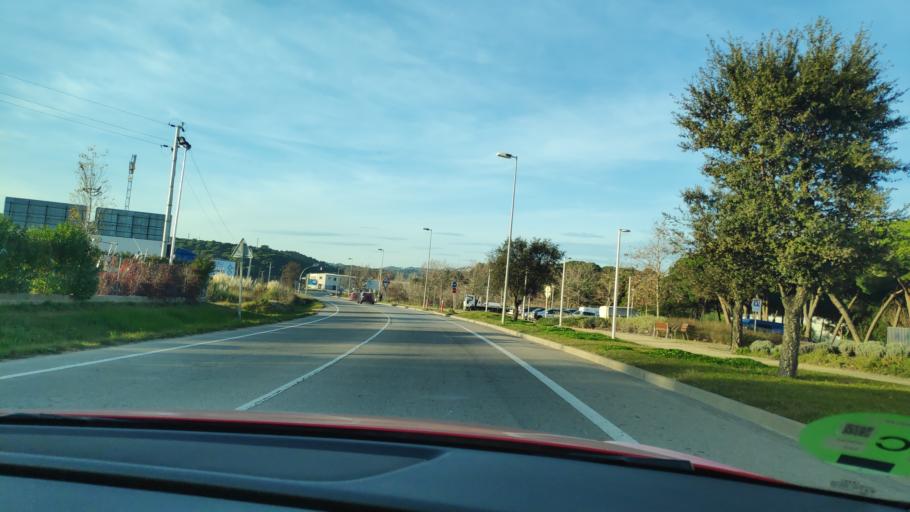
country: ES
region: Catalonia
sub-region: Provincia de Girona
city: Lloret de Mar
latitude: 41.7069
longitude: 2.8347
